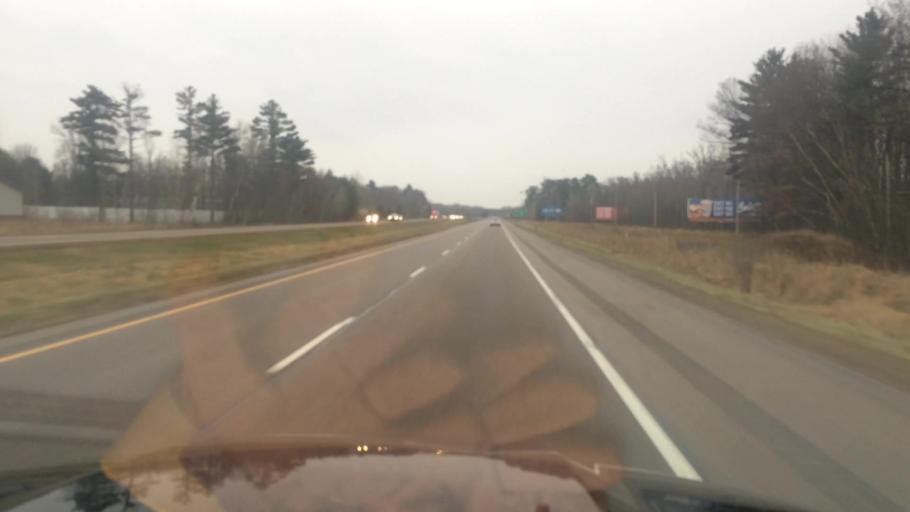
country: US
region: Wisconsin
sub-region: Portage County
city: Stevens Point
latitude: 44.5575
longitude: -89.5881
